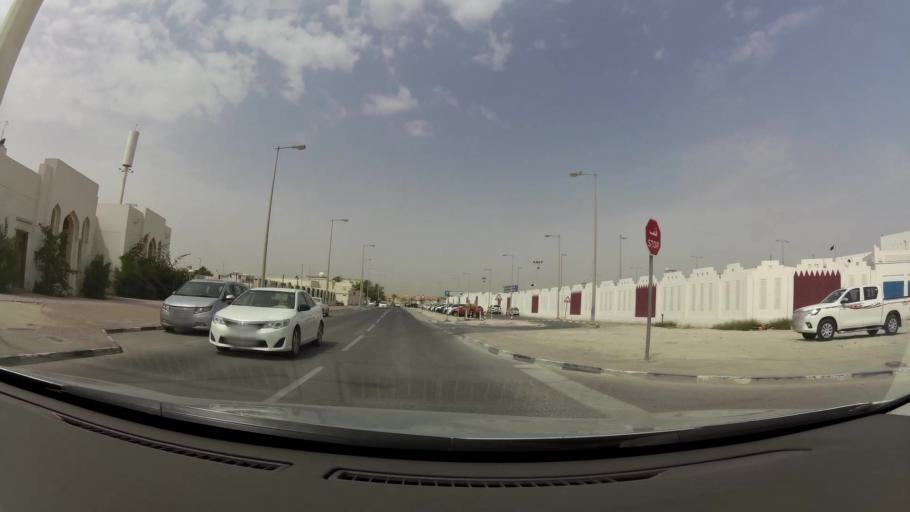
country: QA
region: Baladiyat ad Dawhah
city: Doha
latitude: 25.3021
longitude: 51.4924
